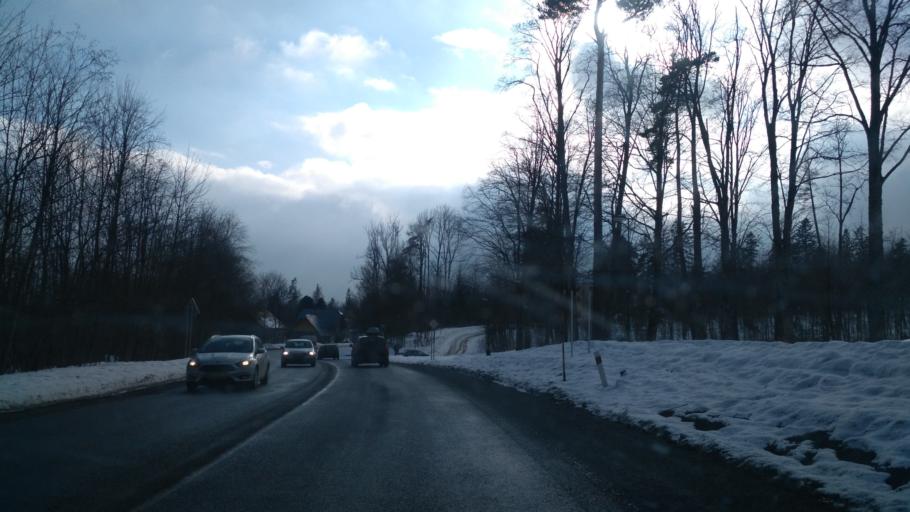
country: SK
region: Presovsky
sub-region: Okres Poprad
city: Nova Lesna
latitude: 49.1699
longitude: 20.2869
